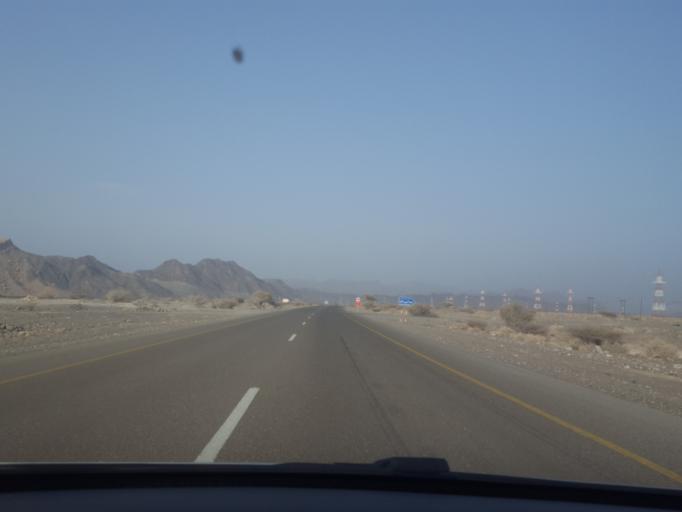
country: AE
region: Abu Dhabi
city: Al Ain
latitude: 24.0459
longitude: 56.0386
